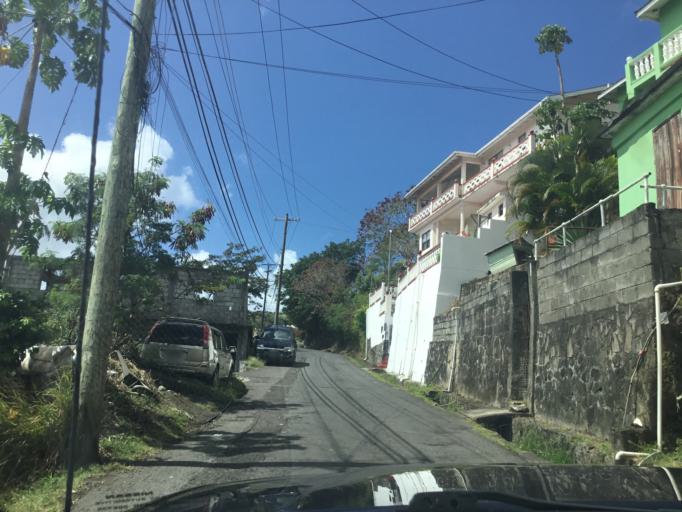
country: VC
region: Saint George
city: Kingstown Park
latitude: 13.1616
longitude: -61.2355
